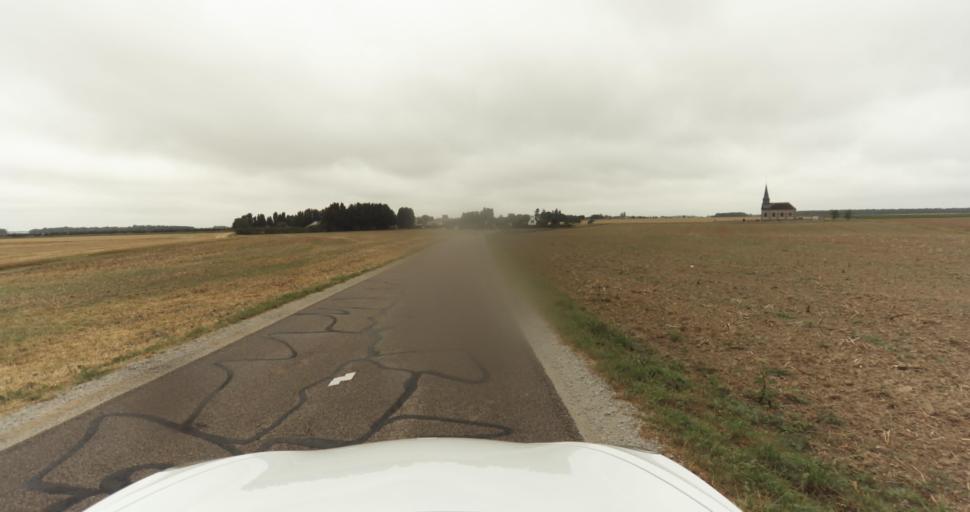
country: FR
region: Haute-Normandie
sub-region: Departement de l'Eure
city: Aviron
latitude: 49.0694
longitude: 1.1078
